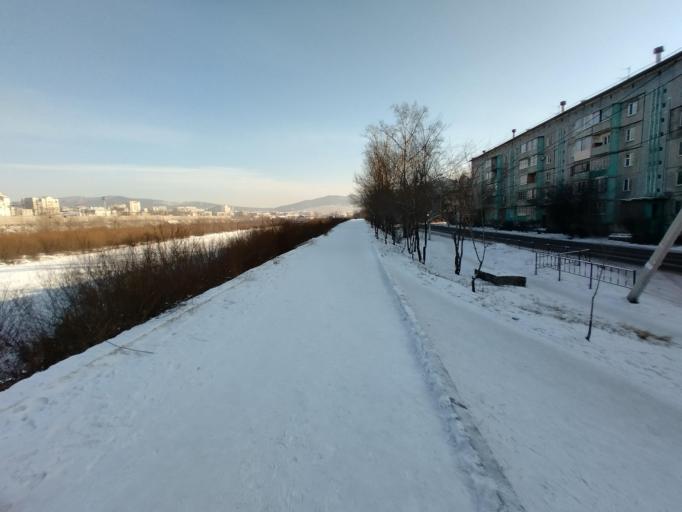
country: RU
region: Transbaikal Territory
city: Chita
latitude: 52.0258
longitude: 113.4939
